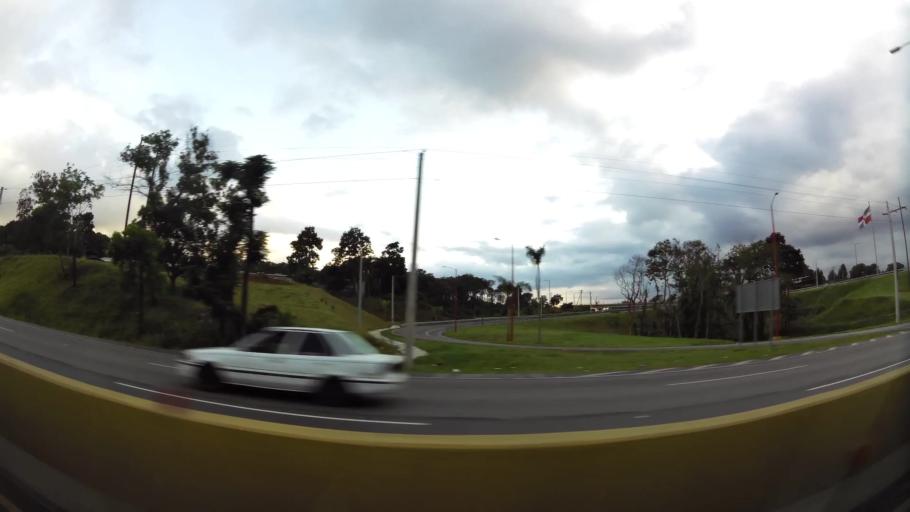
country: DO
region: Santo Domingo
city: Santo Domingo Oeste
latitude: 18.5623
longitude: -70.0681
